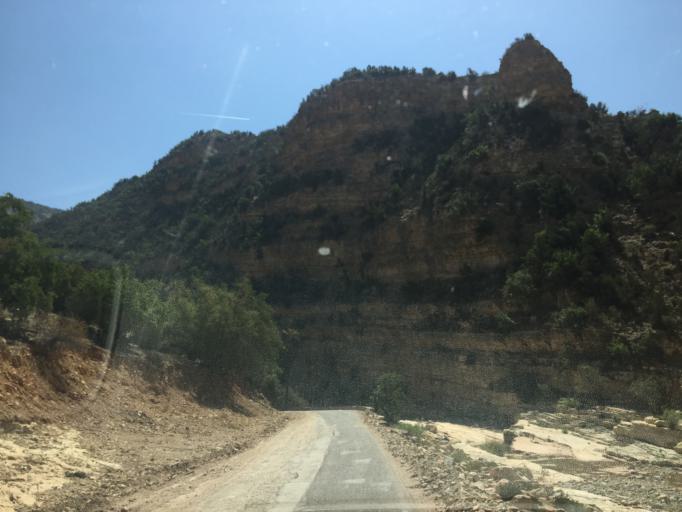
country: MA
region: Souss-Massa-Draa
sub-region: Agadir-Ida-ou-Tnan
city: Aourir
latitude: 30.5642
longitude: -9.5411
